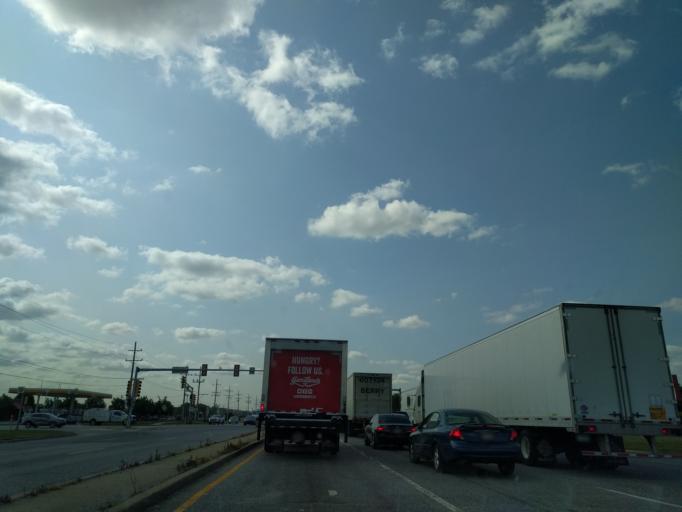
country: US
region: Illinois
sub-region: Cook County
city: Elk Grove Village
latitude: 42.0231
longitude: -87.9599
